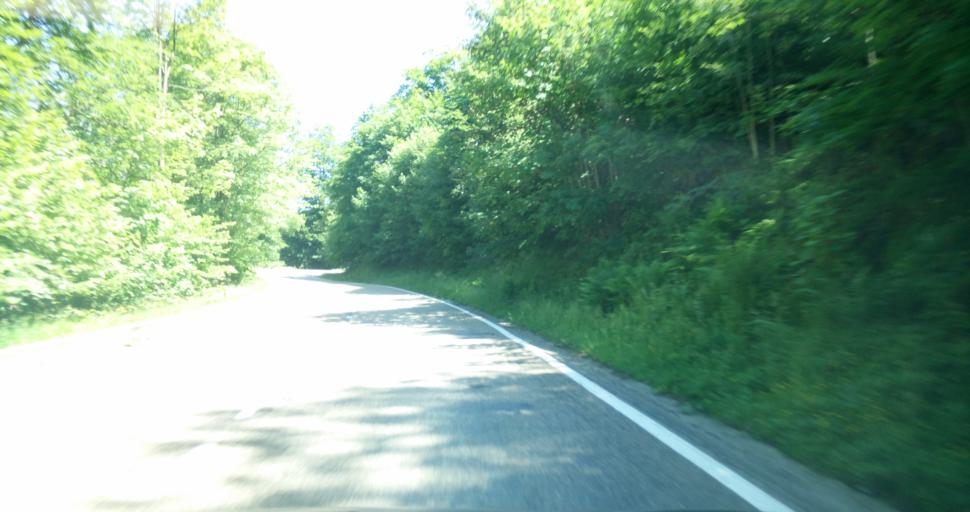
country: BE
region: Wallonia
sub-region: Province du Luxembourg
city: La Roche-en-Ardenne
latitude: 50.2084
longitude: 5.5947
